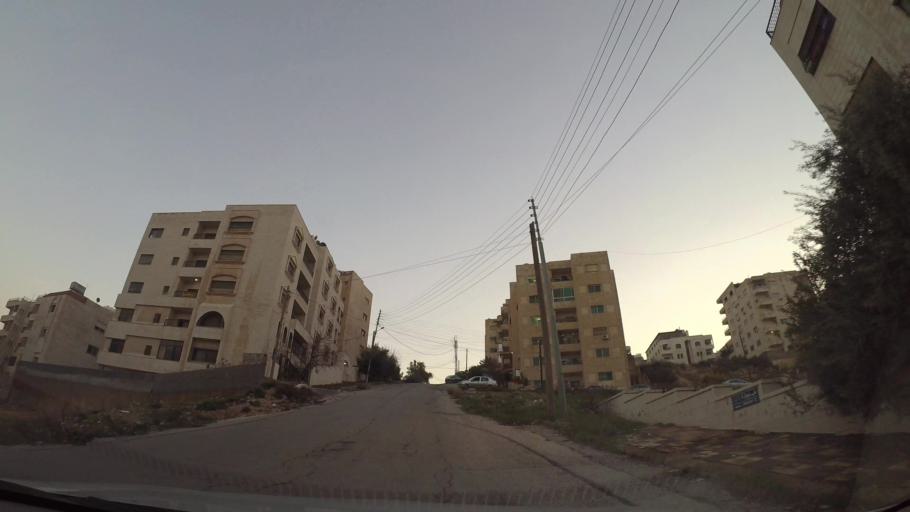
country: JO
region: Amman
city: Al Jubayhah
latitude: 32.0005
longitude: 35.8563
